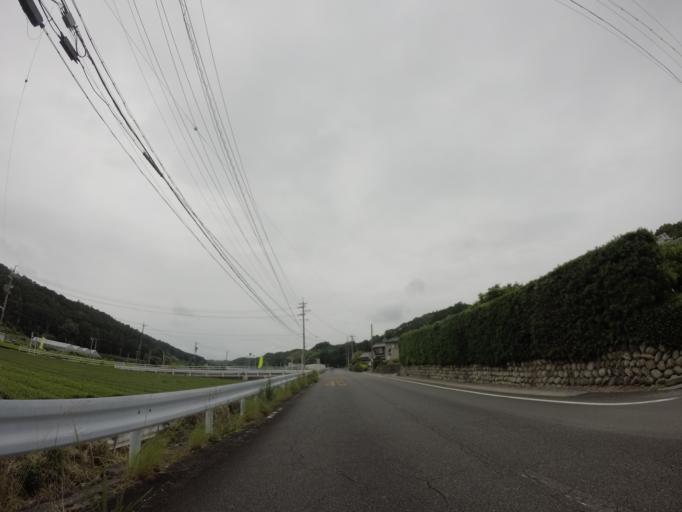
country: JP
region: Shizuoka
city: Shimada
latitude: 34.8065
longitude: 138.1756
